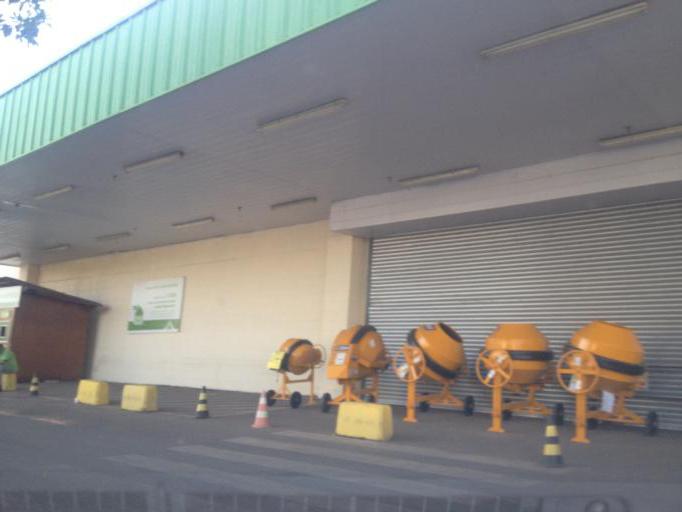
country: BR
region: Federal District
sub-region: Brasilia
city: Brasilia
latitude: -15.7523
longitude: -47.9277
